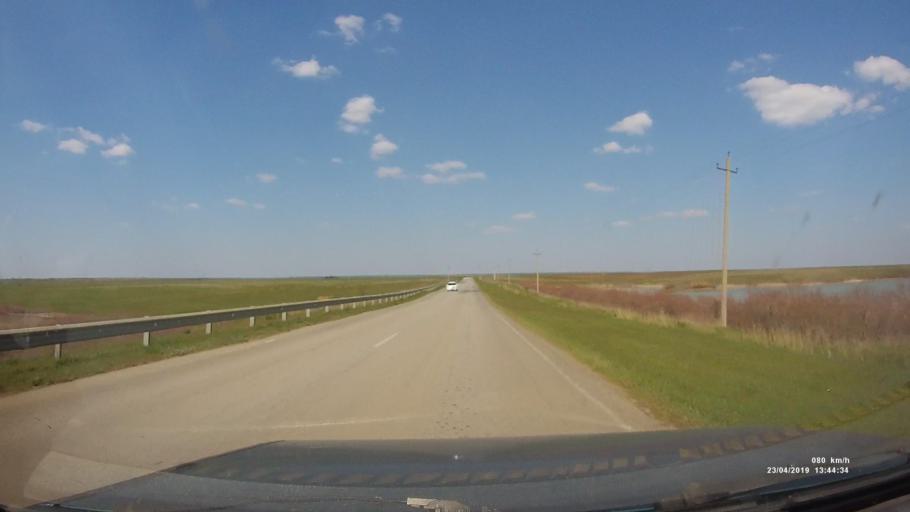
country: RU
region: Kalmykiya
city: Yashalta
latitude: 46.5809
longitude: 42.8173
